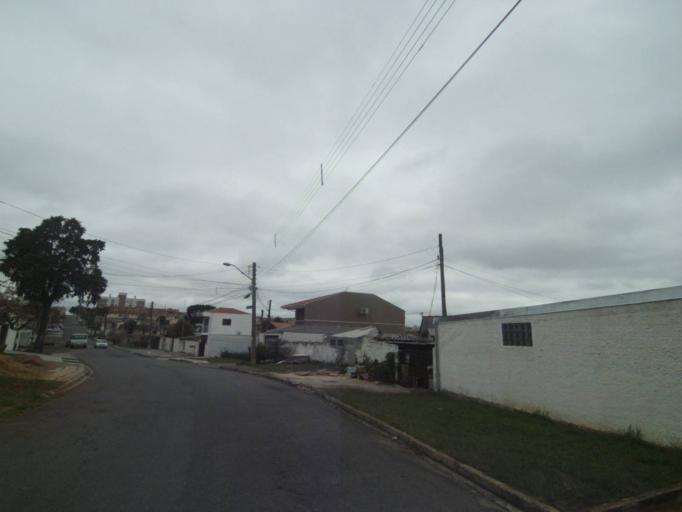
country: BR
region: Parana
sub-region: Curitiba
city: Curitiba
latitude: -25.4987
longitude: -49.2889
